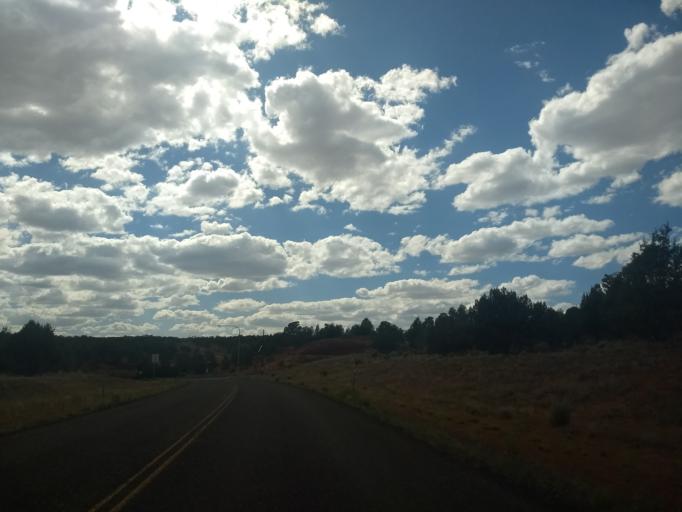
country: US
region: Utah
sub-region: Kane County
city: Kanab
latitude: 37.1455
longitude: -112.5667
